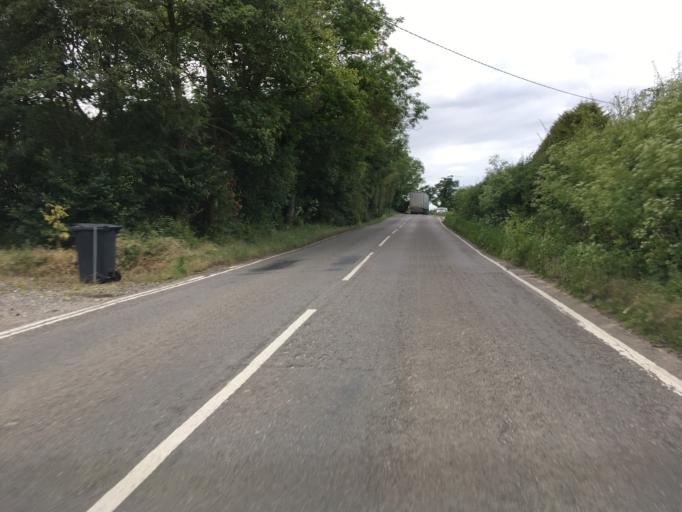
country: GB
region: England
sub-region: Central Bedfordshire
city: Potsgrove
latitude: 51.9674
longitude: -0.6429
